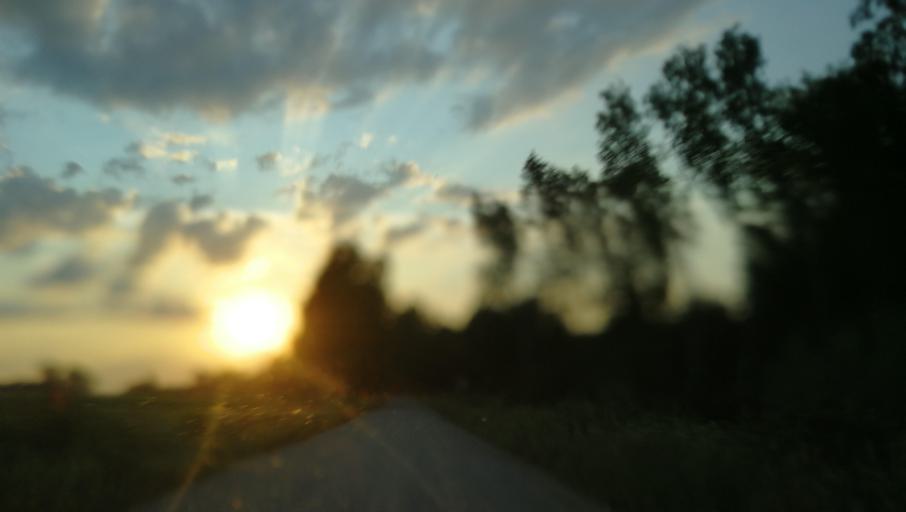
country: LV
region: Amatas Novads
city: Drabesi
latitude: 57.2551
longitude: 25.1680
